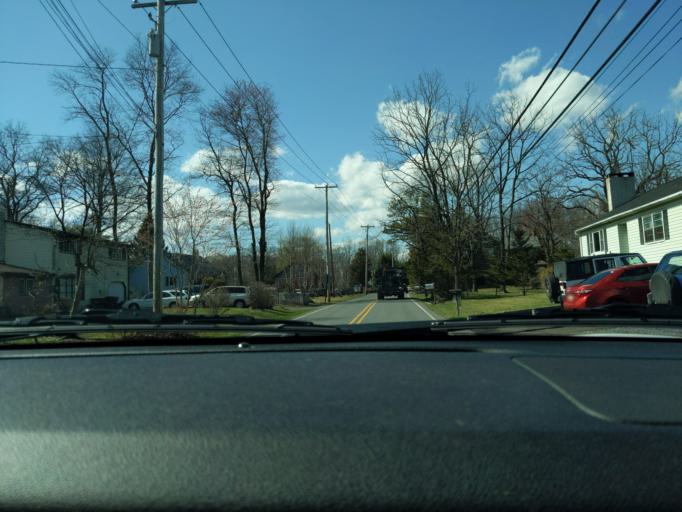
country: US
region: Pennsylvania
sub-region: Bucks County
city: Richlandtown
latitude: 40.4535
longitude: -75.2606
